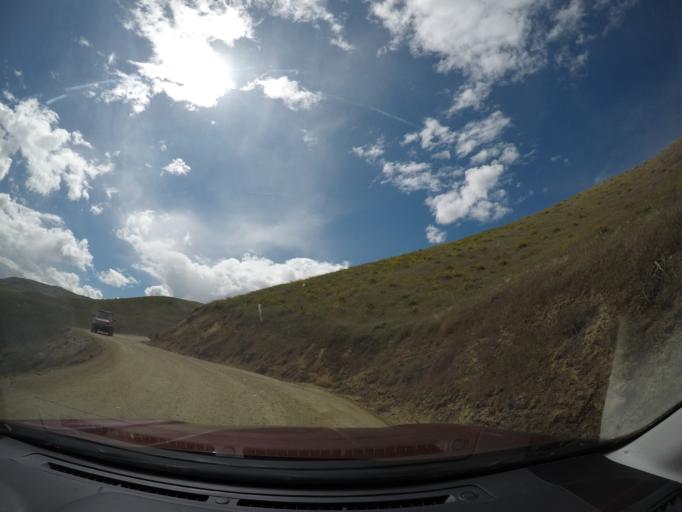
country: US
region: Washington
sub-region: Chelan County
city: West Wenatchee
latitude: 47.4633
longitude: -120.3744
